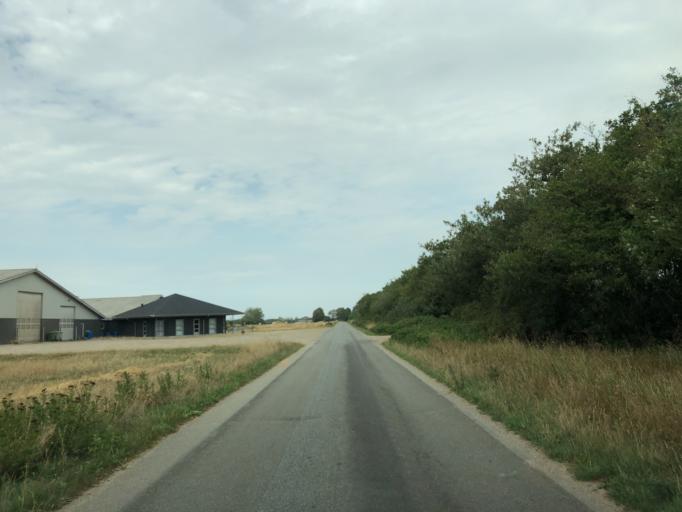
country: DK
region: Central Jutland
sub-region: Holstebro Kommune
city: Ulfborg
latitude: 56.2090
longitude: 8.3168
